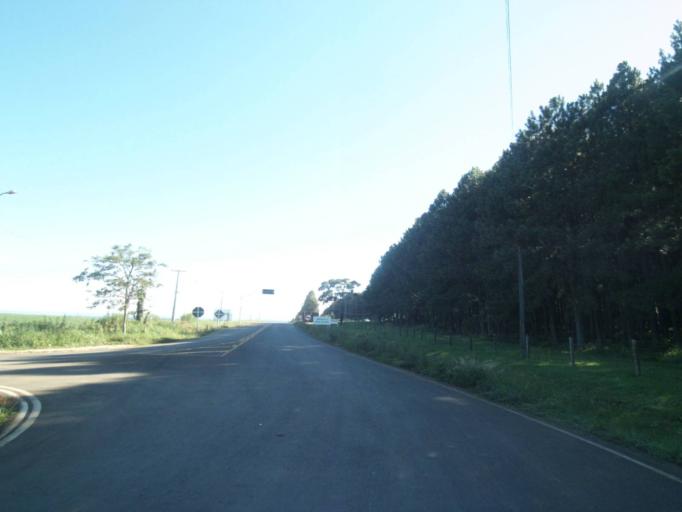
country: BR
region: Parana
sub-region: Pinhao
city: Pinhao
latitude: -25.8349
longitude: -52.0227
